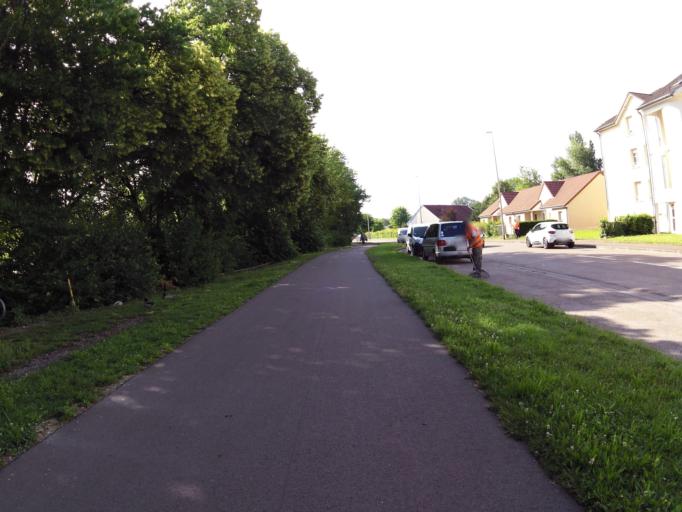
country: FR
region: Champagne-Ardenne
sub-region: Departement de l'Aube
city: Saint-Julien-les-Villas
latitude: 48.2824
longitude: 4.0930
